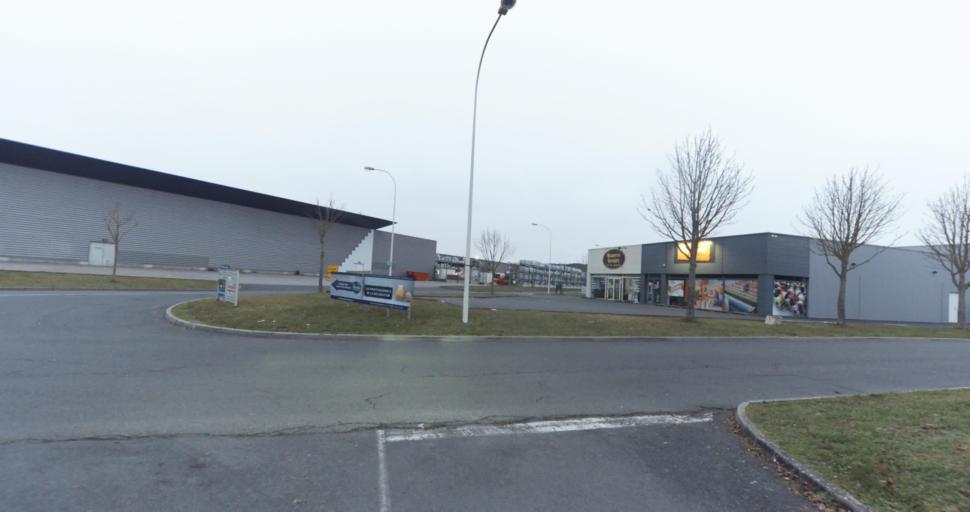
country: FR
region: Pays de la Loire
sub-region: Departement de Maine-et-Loire
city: Distre
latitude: 47.2311
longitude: -0.1178
